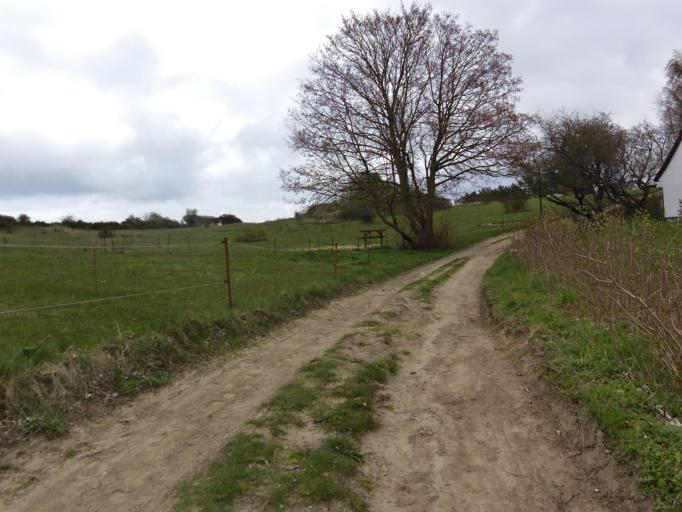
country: DE
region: Mecklenburg-Vorpommern
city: Hiddensee
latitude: 54.5896
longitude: 13.1081
